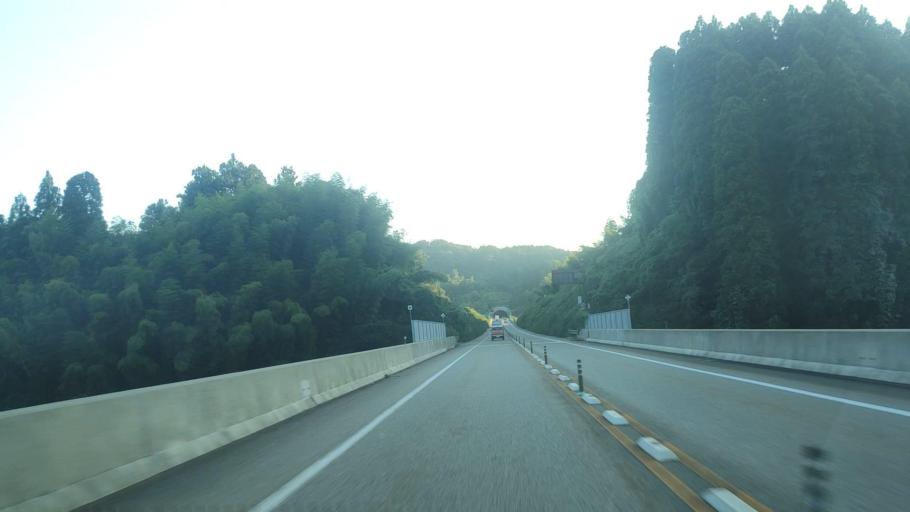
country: JP
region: Toyama
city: Himi
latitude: 36.8972
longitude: 136.9874
